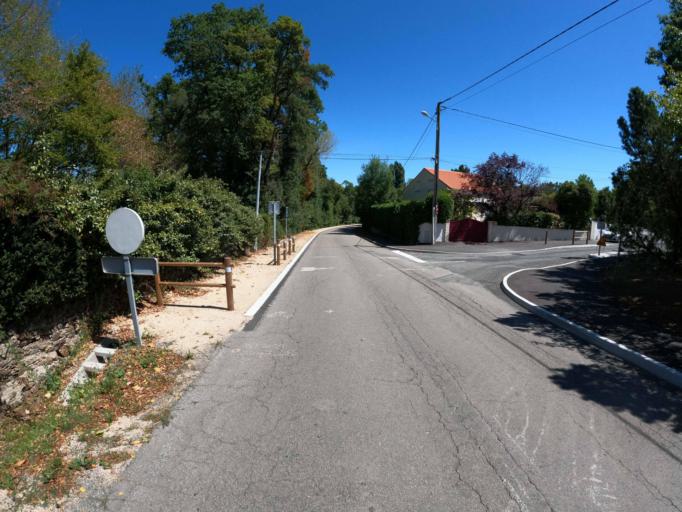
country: FR
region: Pays de la Loire
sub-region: Departement de la Loire-Atlantique
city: La Limouziniere
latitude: 46.9626
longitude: -1.5873
